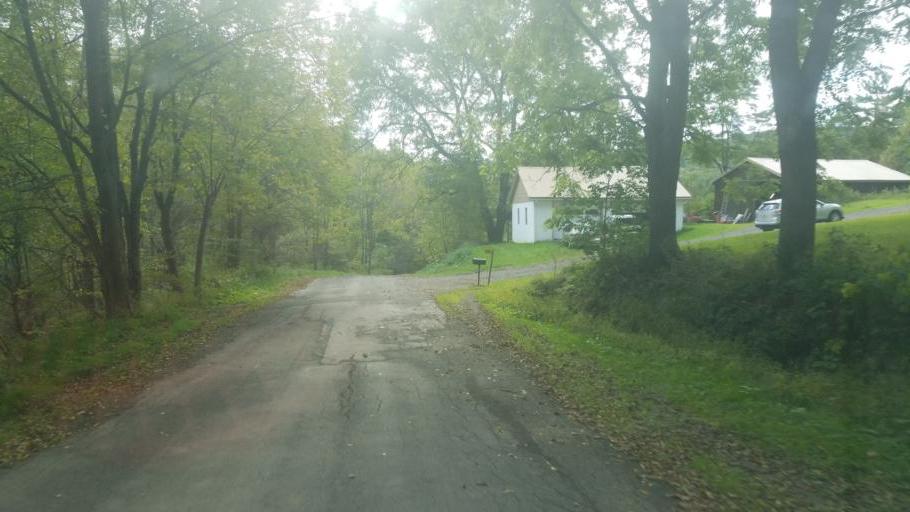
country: US
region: New York
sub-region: Allegany County
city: Cuba
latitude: 42.2257
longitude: -78.3438
